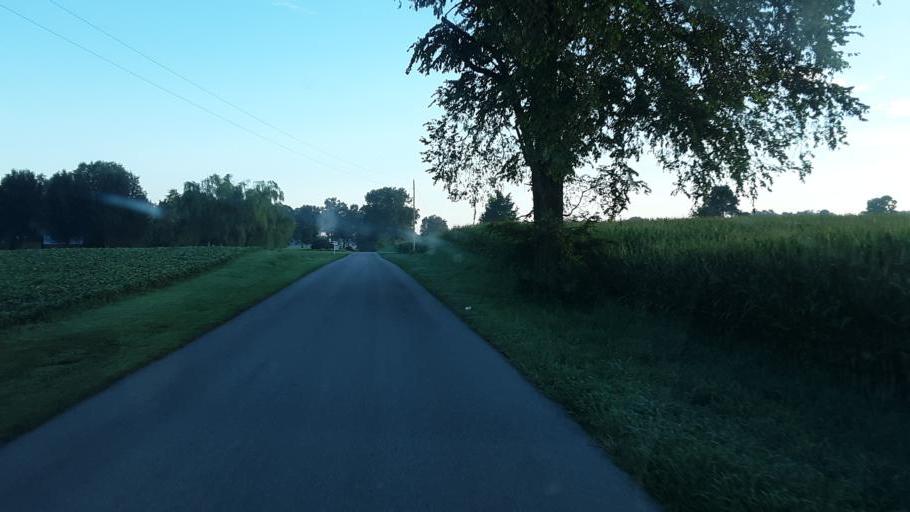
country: US
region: Kentucky
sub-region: Todd County
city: Elkton
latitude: 36.7344
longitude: -87.1674
